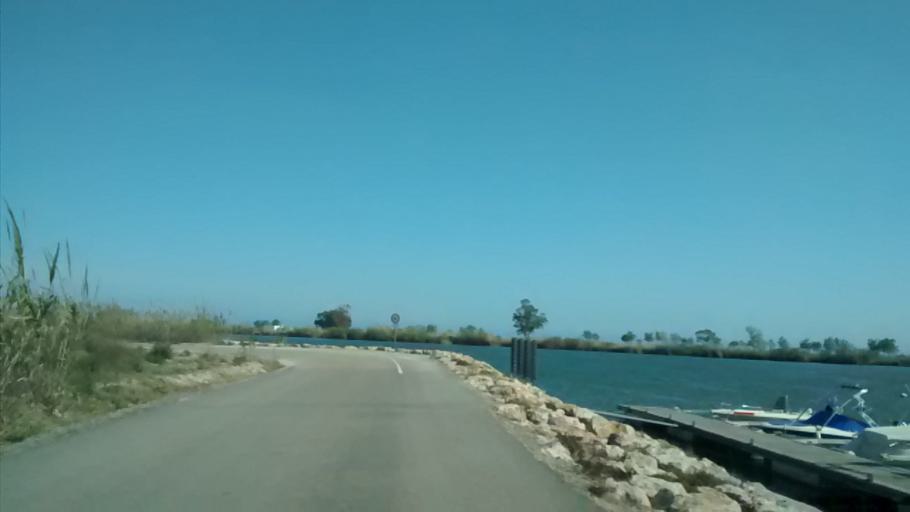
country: ES
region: Catalonia
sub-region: Provincia de Tarragona
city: Deltebre
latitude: 40.7179
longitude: 0.8451
